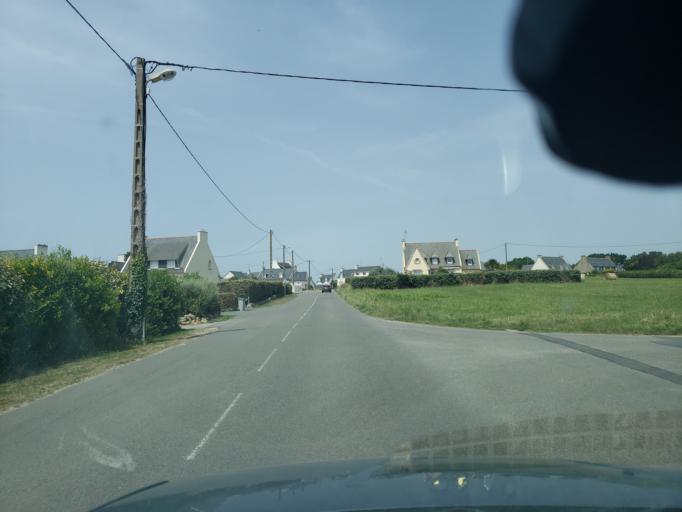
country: FR
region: Brittany
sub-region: Departement du Finistere
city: Guilvinec
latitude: 47.8053
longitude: -4.3042
